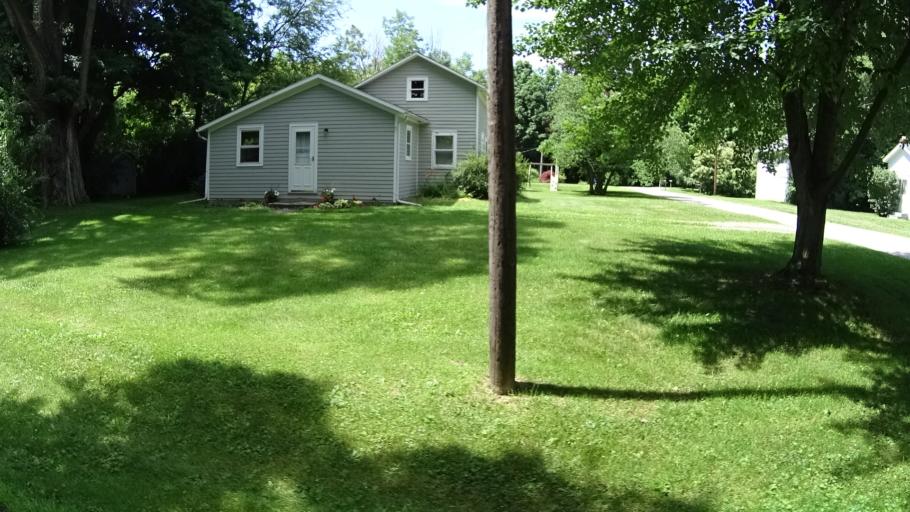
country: US
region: Ohio
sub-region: Erie County
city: Milan
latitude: 41.2951
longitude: -82.6071
